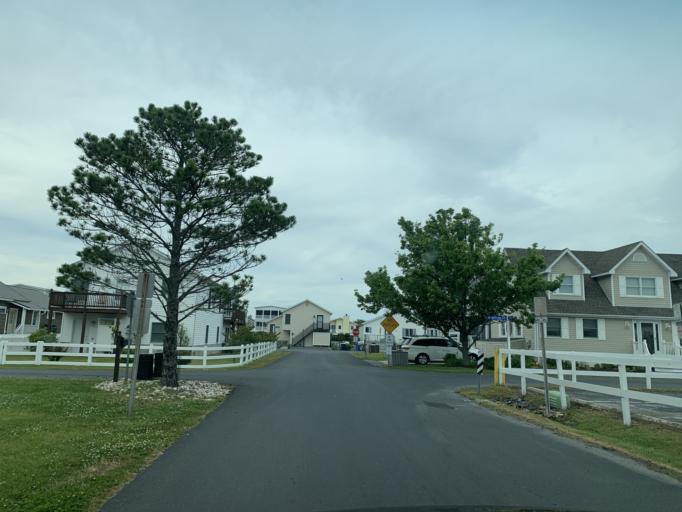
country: US
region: Delaware
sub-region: Sussex County
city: Bethany Beach
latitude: 38.4533
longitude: -75.0535
